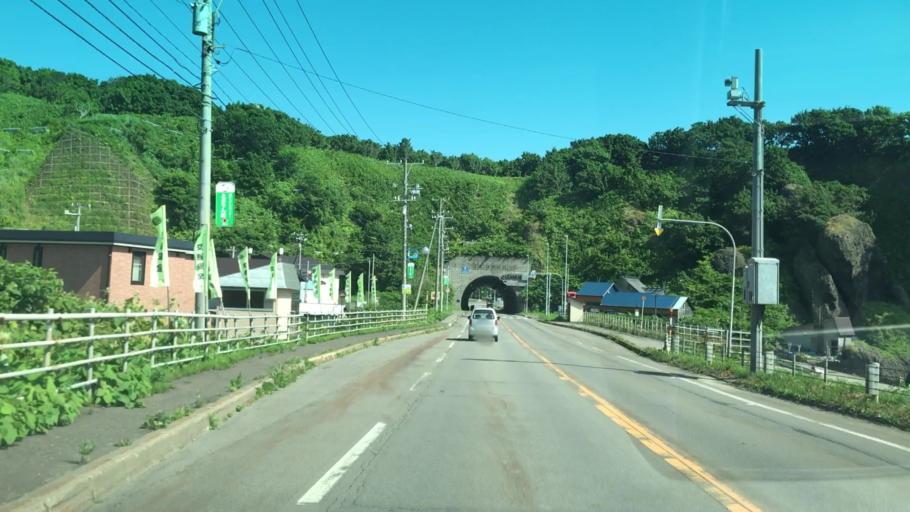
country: JP
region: Hokkaido
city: Iwanai
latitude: 43.0450
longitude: 140.5058
